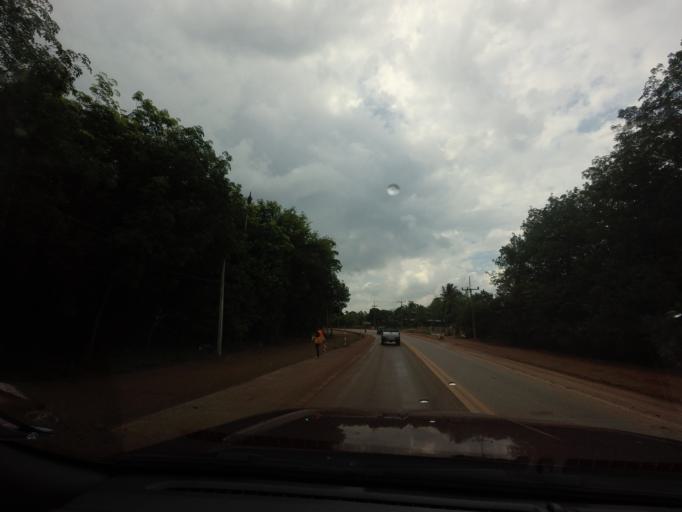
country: TH
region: Yala
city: Ban Nang Sata
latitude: 6.3242
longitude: 101.3037
